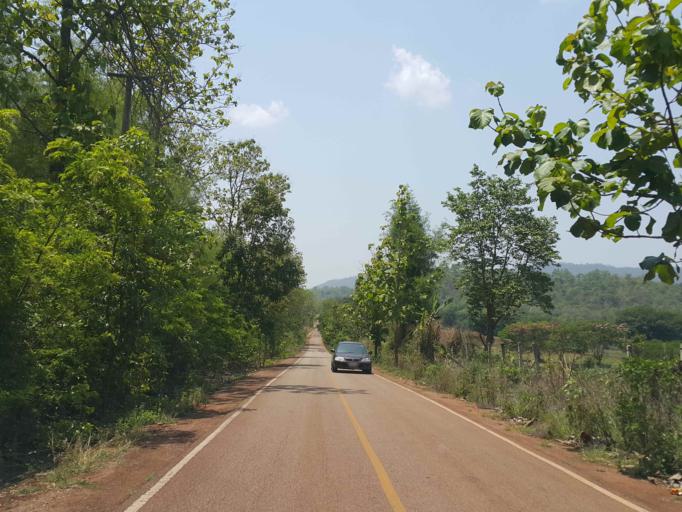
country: TH
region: Chiang Mai
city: Mae Taeng
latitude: 19.0859
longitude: 99.0871
